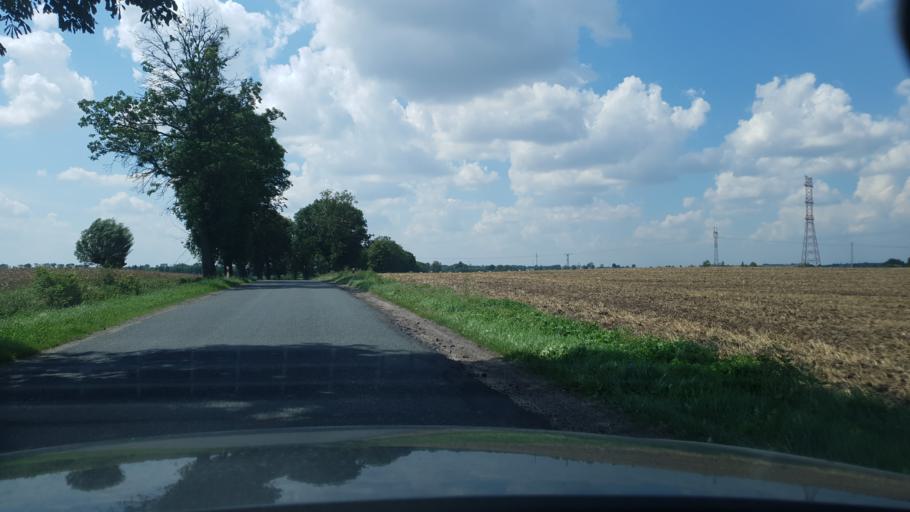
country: PL
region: Kujawsko-Pomorskie
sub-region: Powiat wabrzeski
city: Pluznica
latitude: 53.3732
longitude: 18.8190
